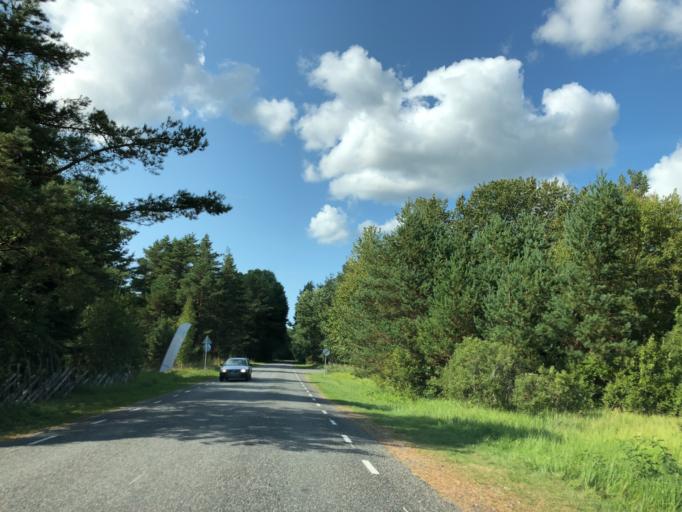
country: EE
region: Hiiumaa
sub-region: Kaerdla linn
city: Kardla
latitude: 58.8073
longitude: 22.7415
